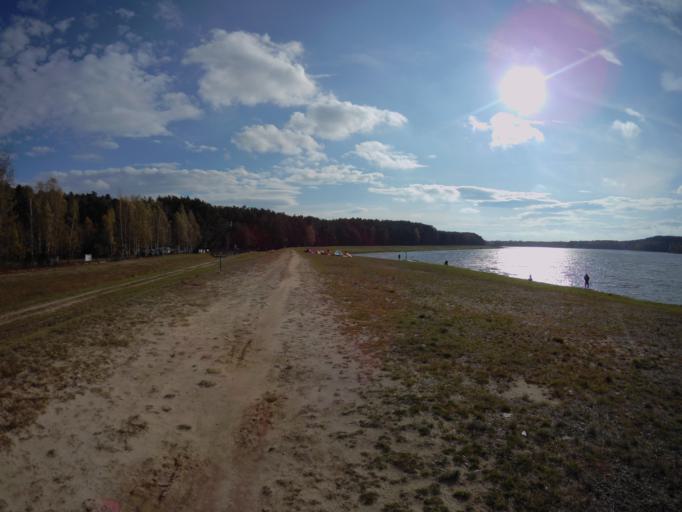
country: PL
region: Subcarpathian Voivodeship
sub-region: Powiat kolbuszowski
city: Lipnica
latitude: 50.3362
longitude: 21.9430
